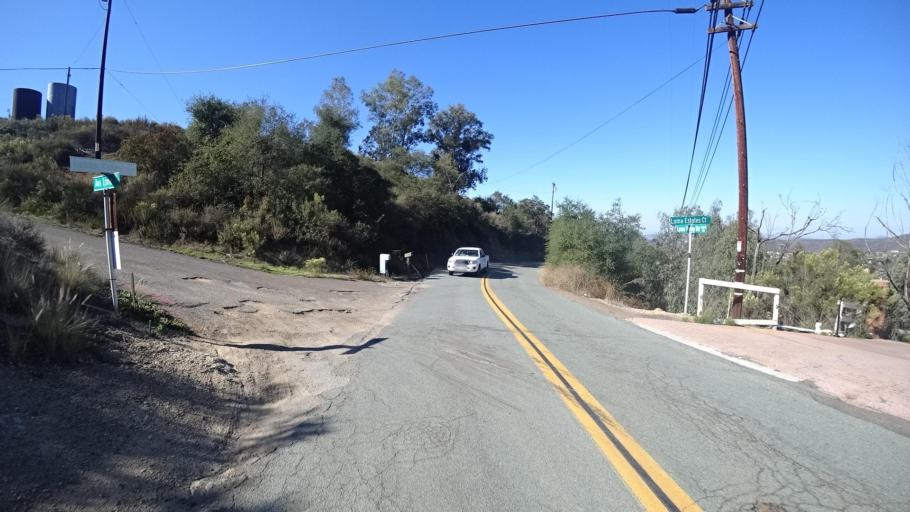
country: US
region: California
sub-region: San Diego County
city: Jamul
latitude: 32.7298
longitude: -116.8310
